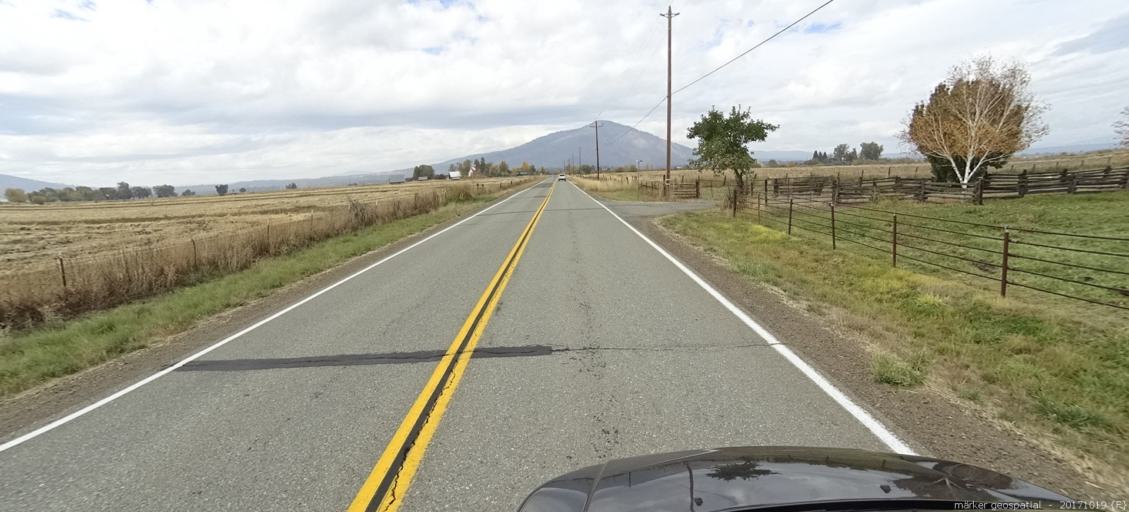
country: US
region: California
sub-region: Shasta County
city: Burney
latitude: 41.0622
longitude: -121.4750
